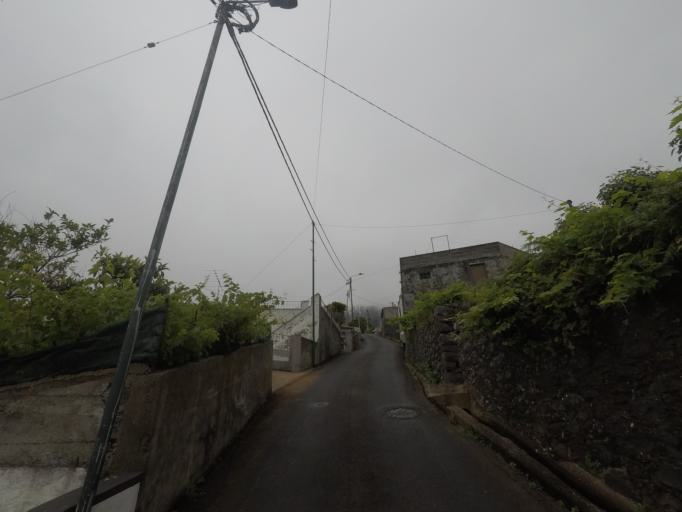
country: PT
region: Madeira
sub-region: Funchal
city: Nossa Senhora do Monte
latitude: 32.6800
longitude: -16.9433
